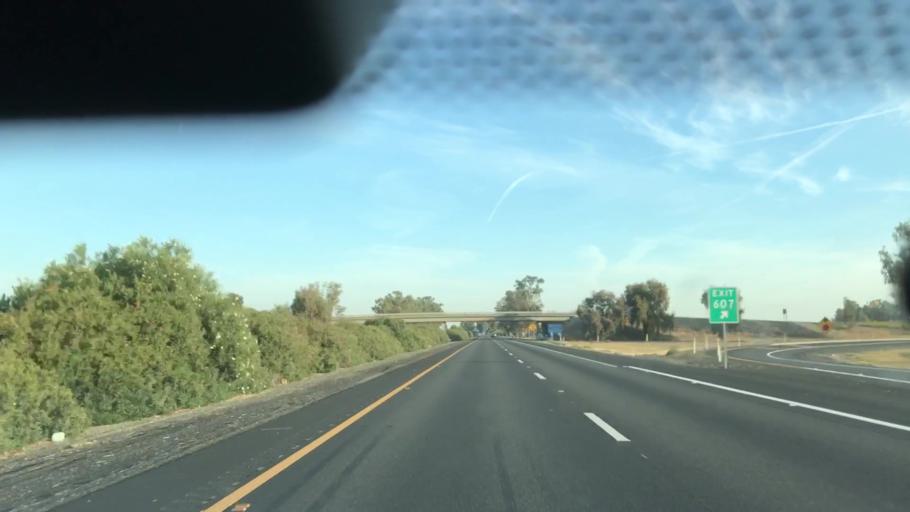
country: US
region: California
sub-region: Glenn County
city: Willows
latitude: 39.5803
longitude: -122.2106
